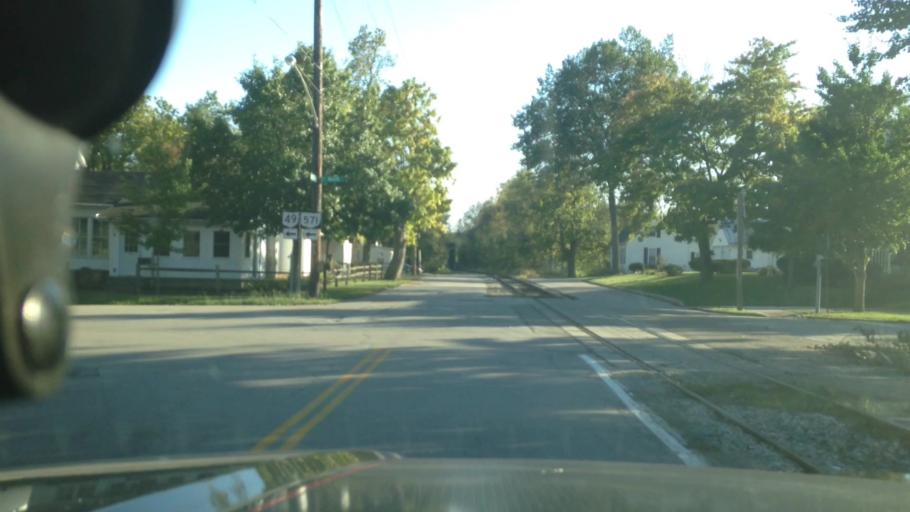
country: US
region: Ohio
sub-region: Darke County
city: Greenville
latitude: 40.1060
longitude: -84.6395
